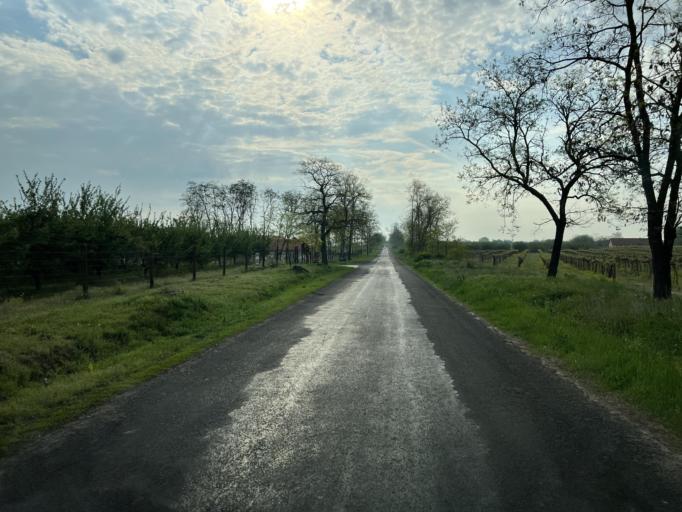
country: HU
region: Pest
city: Cegledbercel
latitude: 47.2164
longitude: 19.7070
